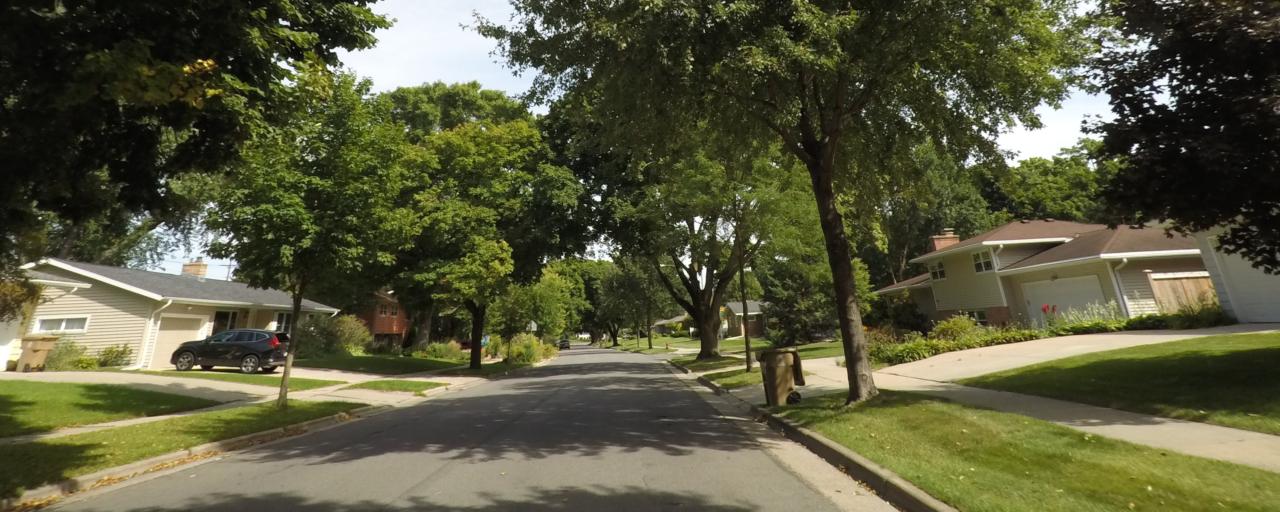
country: US
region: Wisconsin
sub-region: Dane County
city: Shorewood Hills
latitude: 43.0634
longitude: -89.4618
